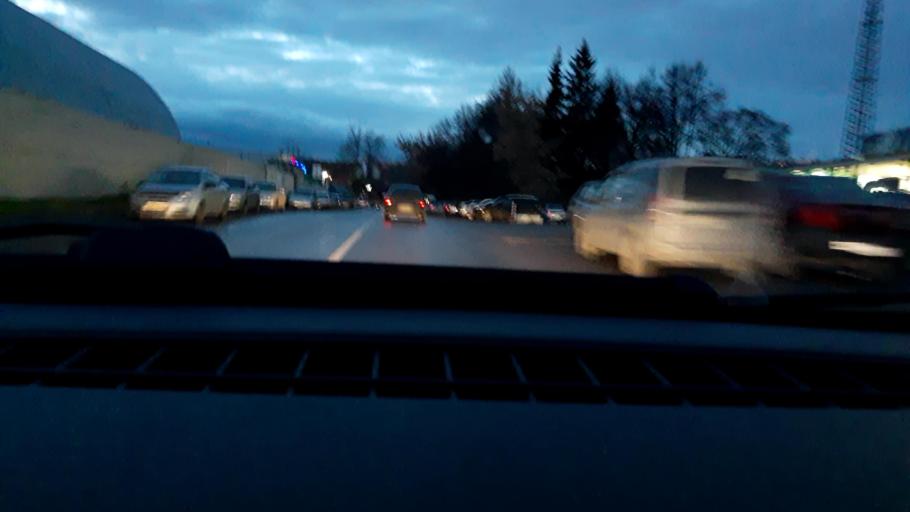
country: RU
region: Bashkortostan
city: Ufa
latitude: 54.8072
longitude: 56.0675
